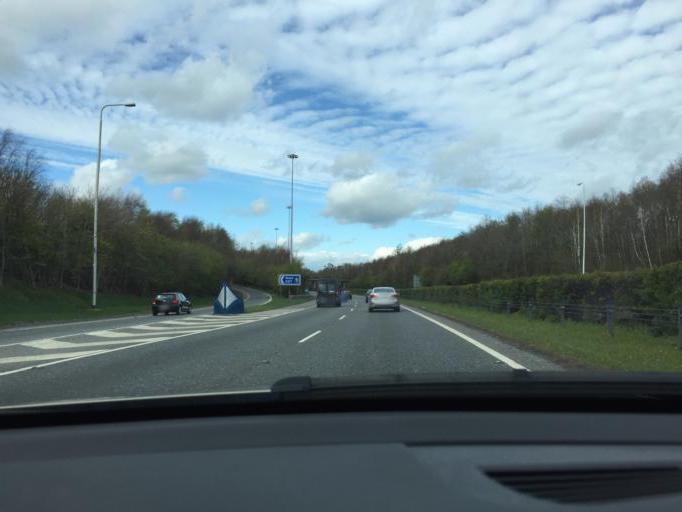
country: IE
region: Leinster
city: Little Bray
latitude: 53.2072
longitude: -6.1258
